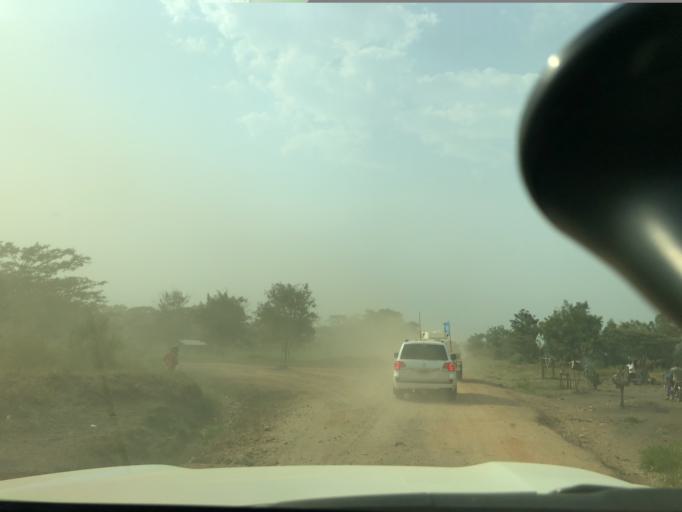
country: UG
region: Western Region
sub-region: Kasese District
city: Kilembe
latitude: 0.0619
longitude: 29.6634
